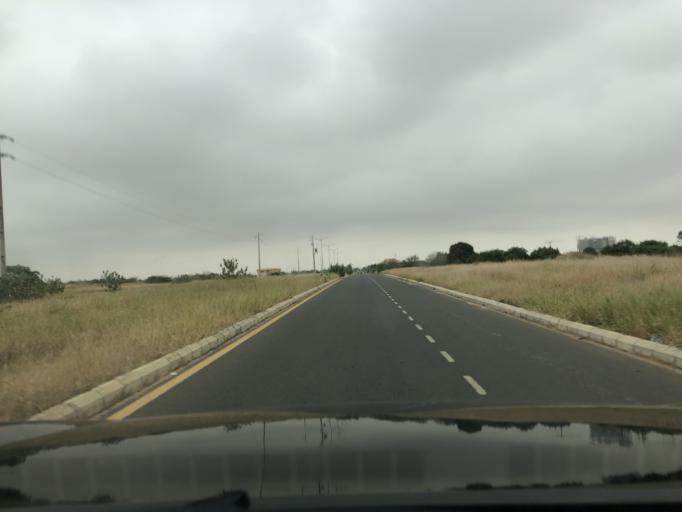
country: AO
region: Luanda
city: Luanda
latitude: -8.9546
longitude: 13.2519
